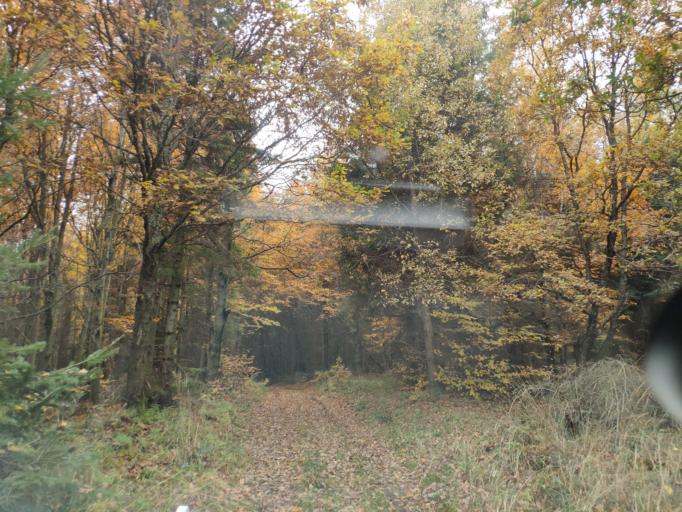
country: SK
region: Kosicky
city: Medzev
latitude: 48.7495
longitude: 20.9844
